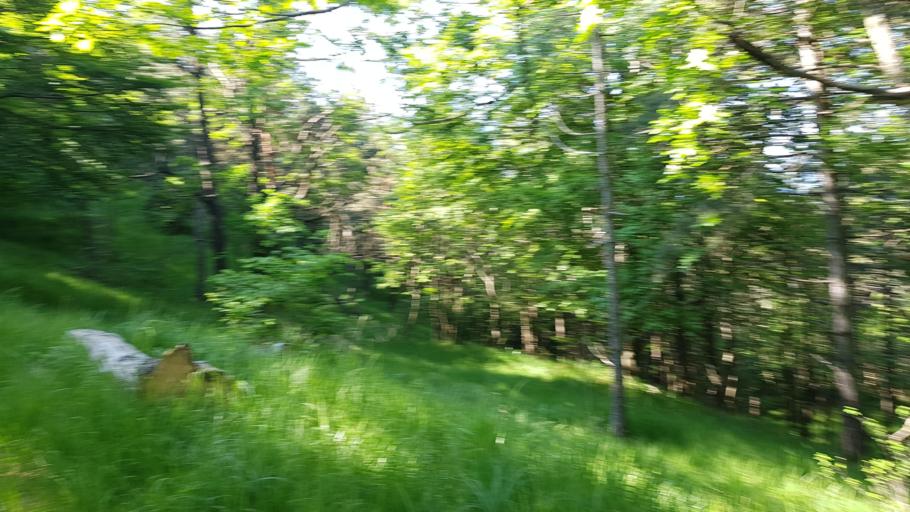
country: IT
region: Friuli Venezia Giulia
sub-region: Provincia di Udine
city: Moggio Udinese
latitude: 46.4272
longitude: 13.1885
